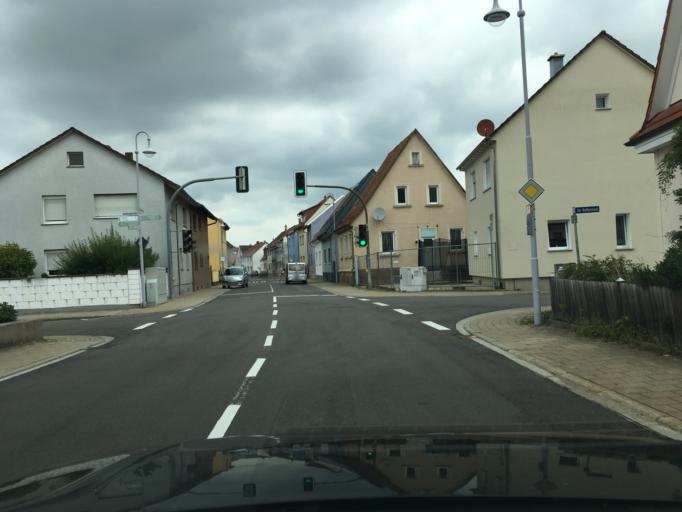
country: DE
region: Baden-Wuerttemberg
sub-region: Karlsruhe Region
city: Sankt Leon-Rot
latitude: 49.2608
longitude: 8.6371
